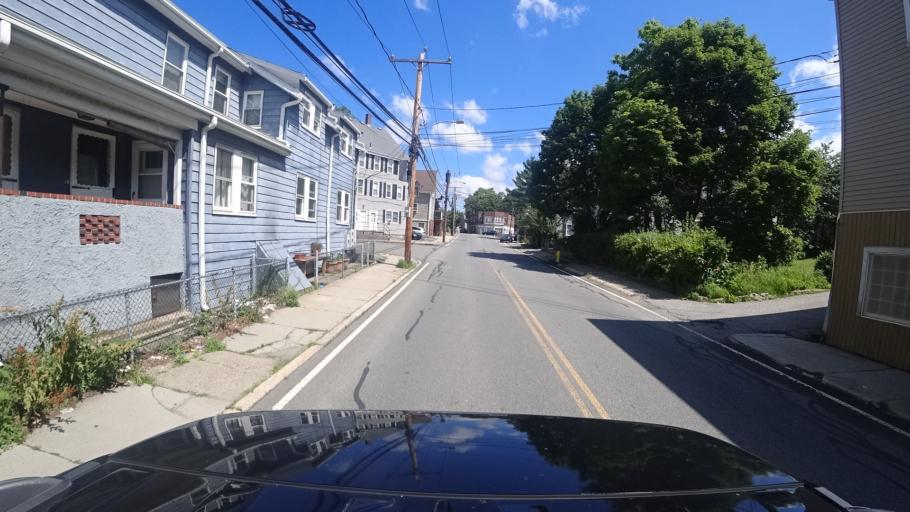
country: US
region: Massachusetts
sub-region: Norfolk County
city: Dedham
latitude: 42.2526
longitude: -71.1555
